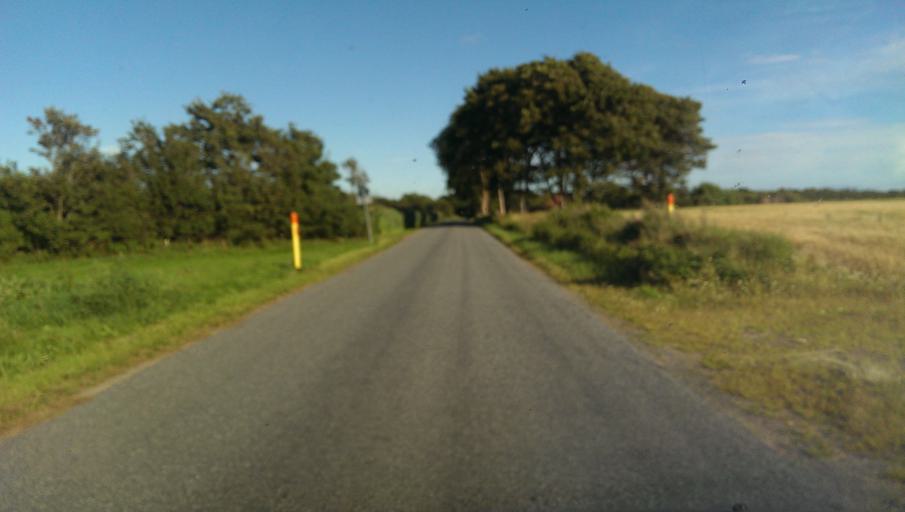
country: DK
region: South Denmark
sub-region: Esbjerg Kommune
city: Esbjerg
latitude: 55.5313
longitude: 8.4859
